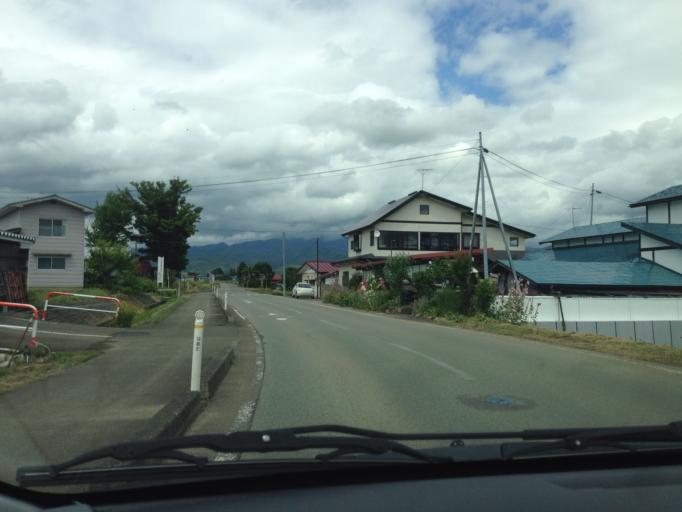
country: JP
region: Fukushima
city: Kitakata
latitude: 37.6227
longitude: 139.9028
